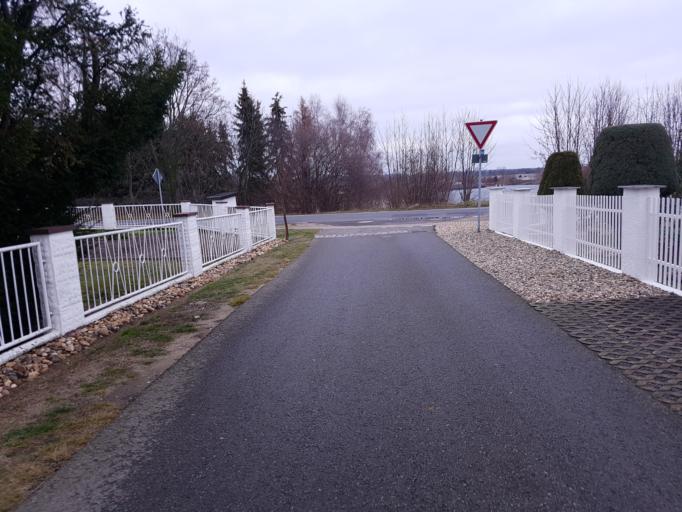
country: DE
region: Brandenburg
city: Groden
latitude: 51.4017
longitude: 13.5805
